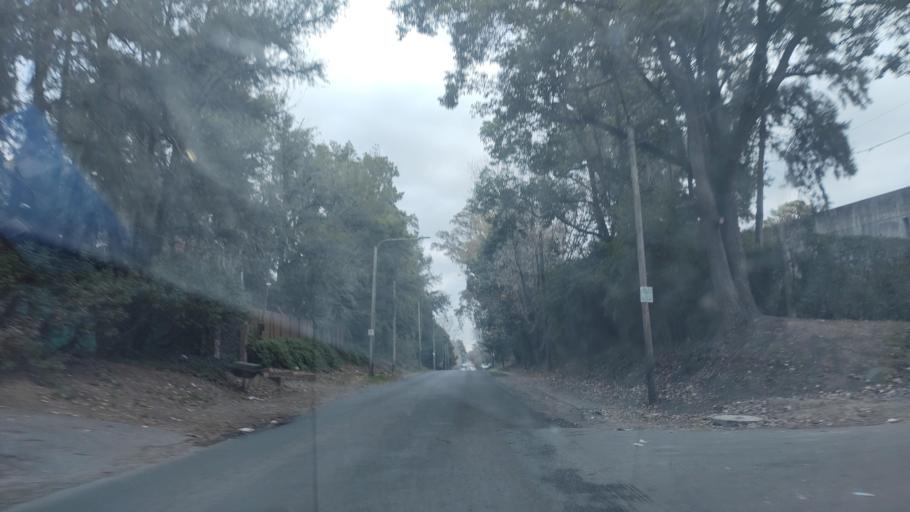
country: AR
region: Buenos Aires
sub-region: Partido de La Plata
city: La Plata
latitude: -34.8609
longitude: -58.0877
